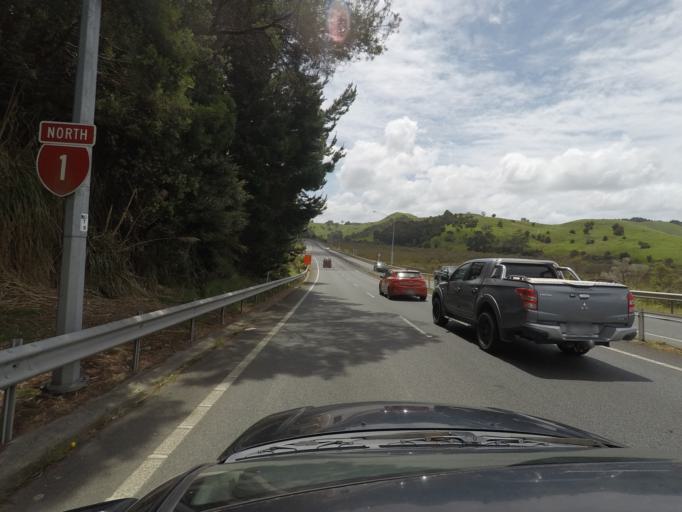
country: NZ
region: Auckland
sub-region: Auckland
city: Warkworth
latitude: -36.5290
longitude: 174.6777
